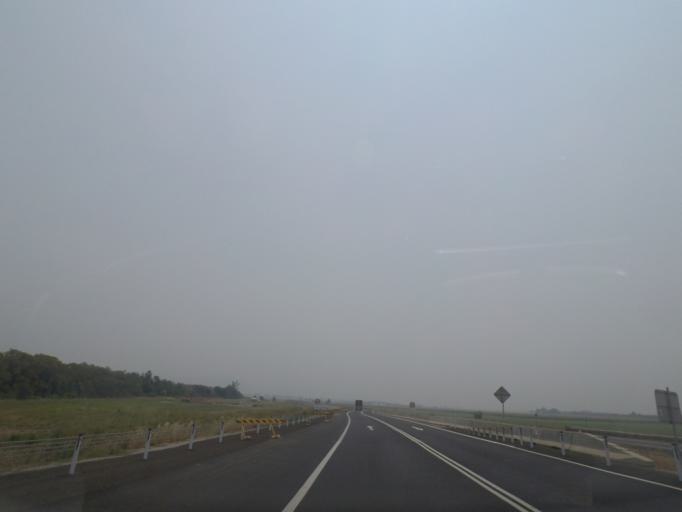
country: AU
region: New South Wales
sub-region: Clarence Valley
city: Maclean
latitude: -29.4043
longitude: 153.2425
